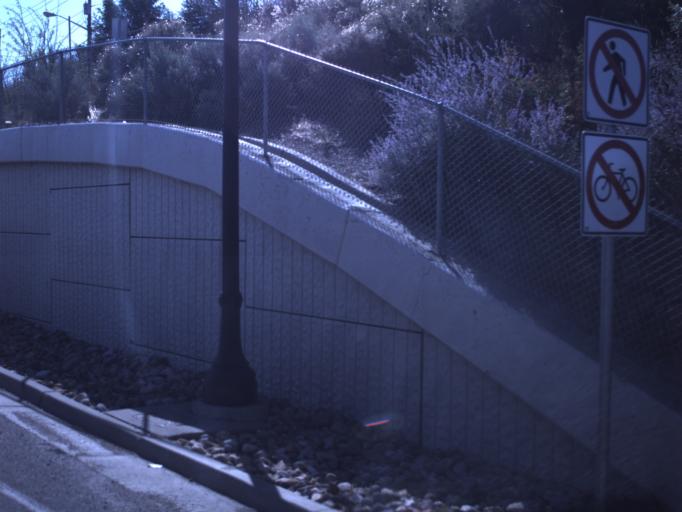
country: US
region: Utah
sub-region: Salt Lake County
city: Murray
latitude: 40.6744
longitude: -111.8985
